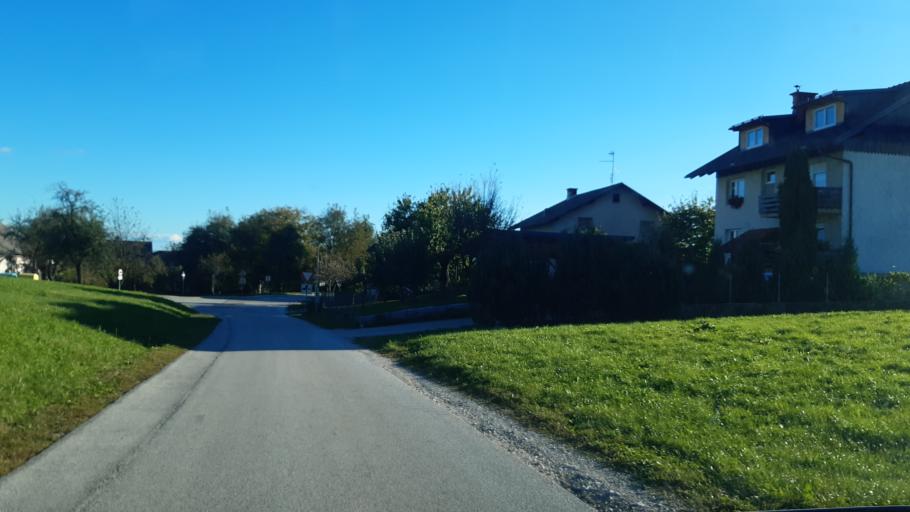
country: SI
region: Kranj
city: Zgornje Bitnje
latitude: 46.2336
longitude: 14.3361
